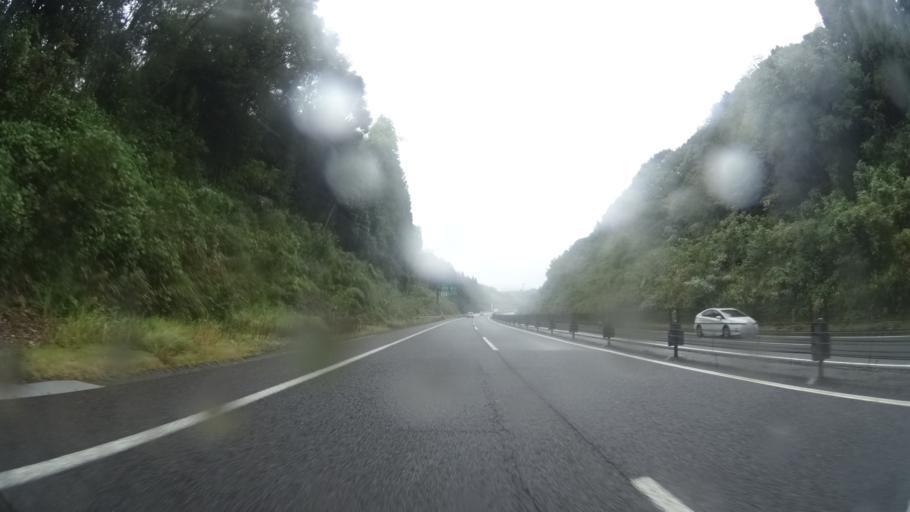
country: JP
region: Kagoshima
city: Okuchi-shinohara
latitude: 31.9376
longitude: 130.7094
